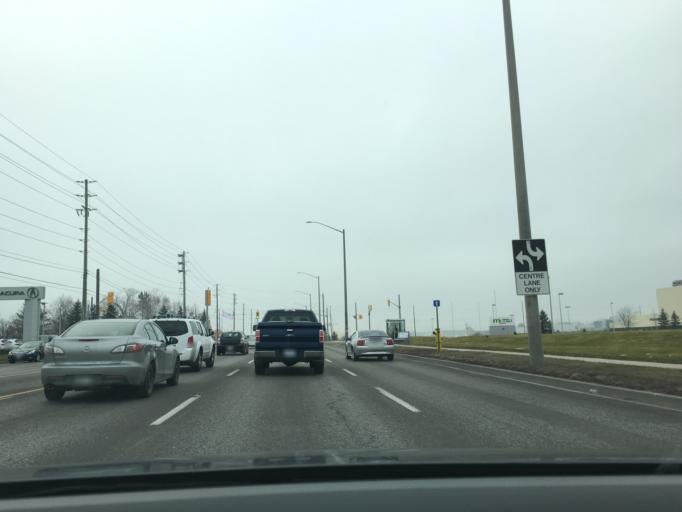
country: CA
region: Ontario
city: Innisfil
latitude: 44.3331
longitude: -79.6951
